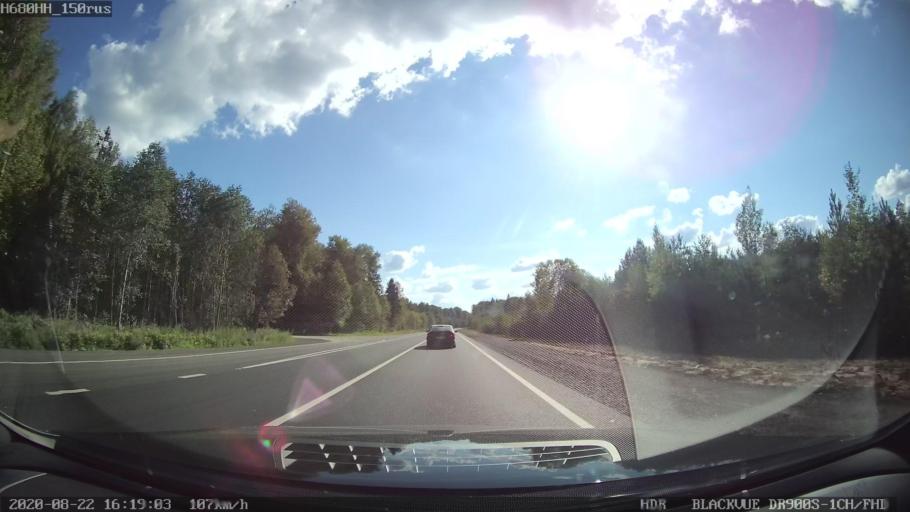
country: RU
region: Tverskaya
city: Rameshki
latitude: 57.4086
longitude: 36.1271
